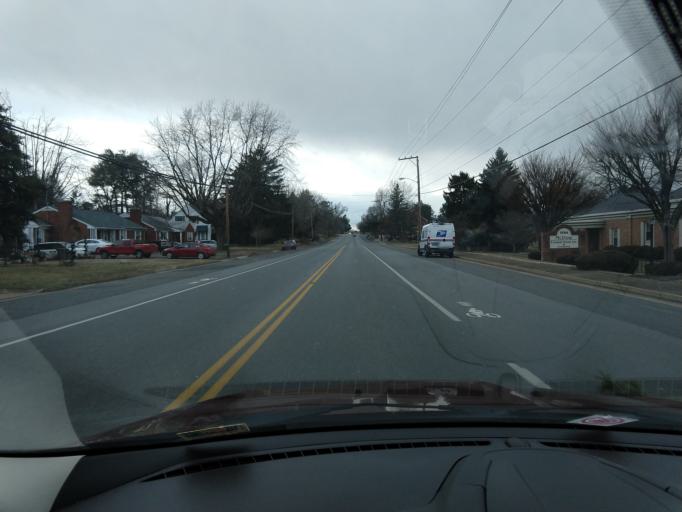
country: US
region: Virginia
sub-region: City of Waynesboro
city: Waynesboro
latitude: 38.0737
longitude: -78.9049
